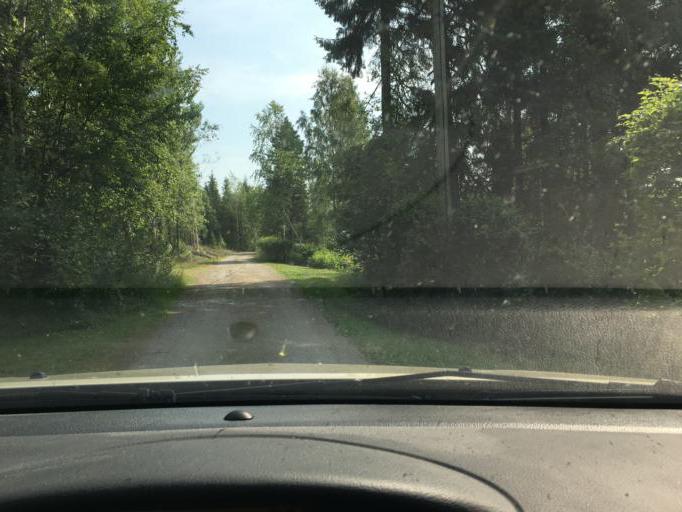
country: SE
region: Norrbotten
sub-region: Kalix Kommun
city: Rolfs
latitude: 65.7578
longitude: 22.9988
